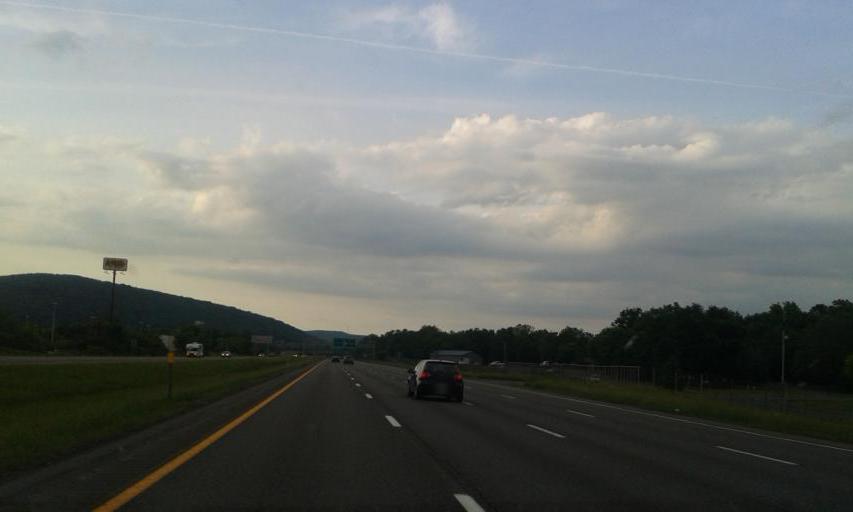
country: US
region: New York
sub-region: Broome County
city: Port Dickinson
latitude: 42.1290
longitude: -75.9040
